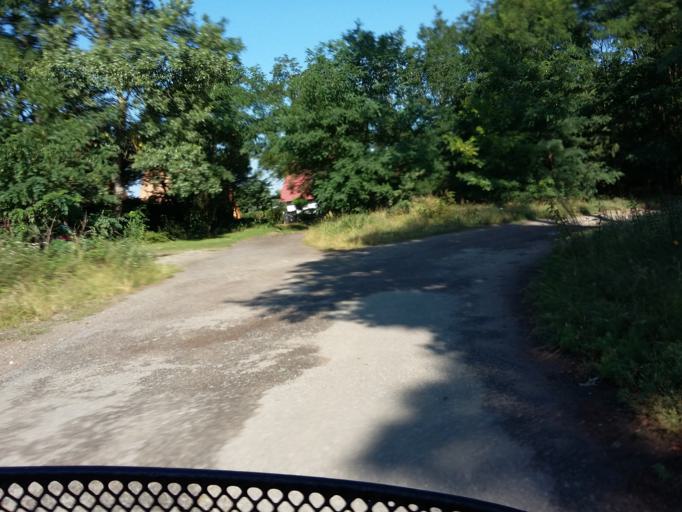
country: AT
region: Lower Austria
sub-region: Politischer Bezirk Ganserndorf
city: Drosing
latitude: 48.4972
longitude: 16.9585
